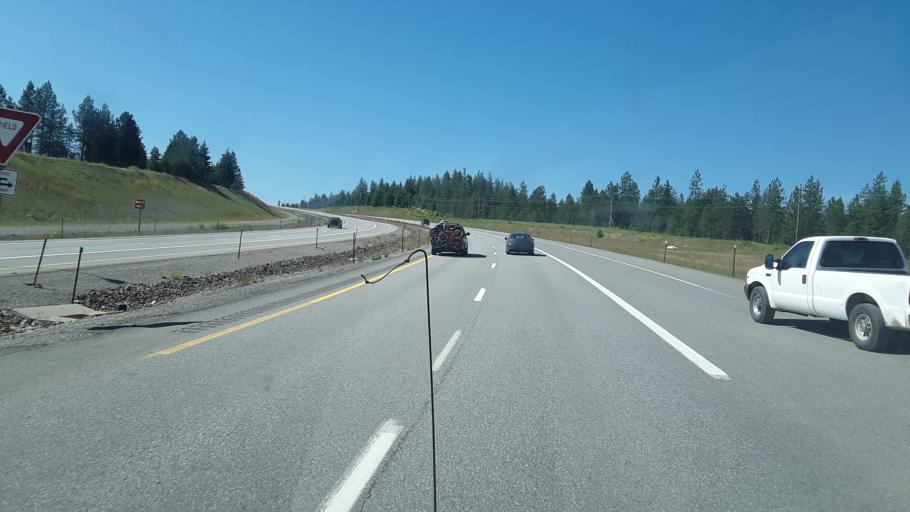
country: US
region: Idaho
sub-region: Kootenai County
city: Spirit Lake
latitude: 47.9864
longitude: -116.6974
